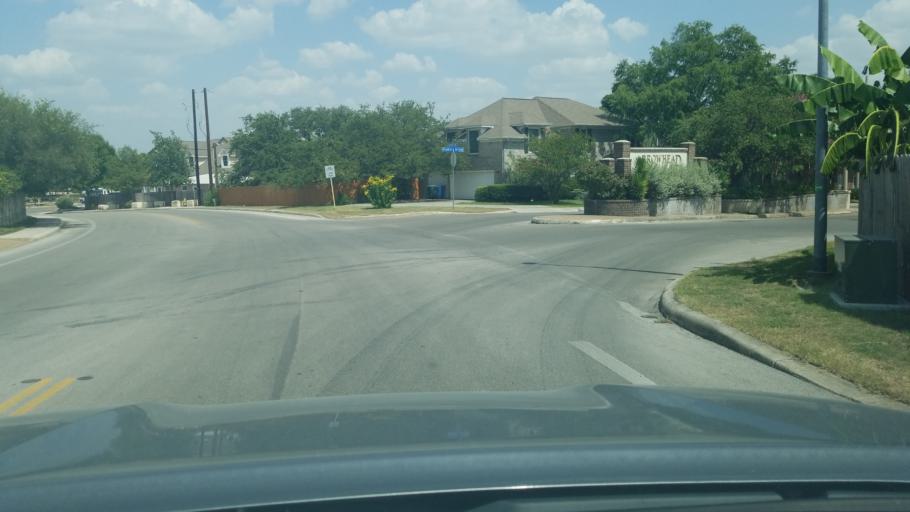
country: US
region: Texas
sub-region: Bexar County
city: Hollywood Park
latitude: 29.6451
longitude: -98.4945
